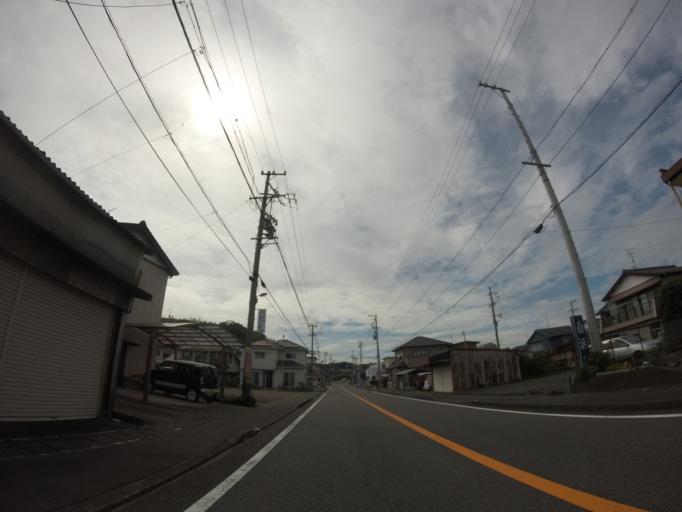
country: JP
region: Shizuoka
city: Sagara
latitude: 34.6796
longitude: 138.1989
